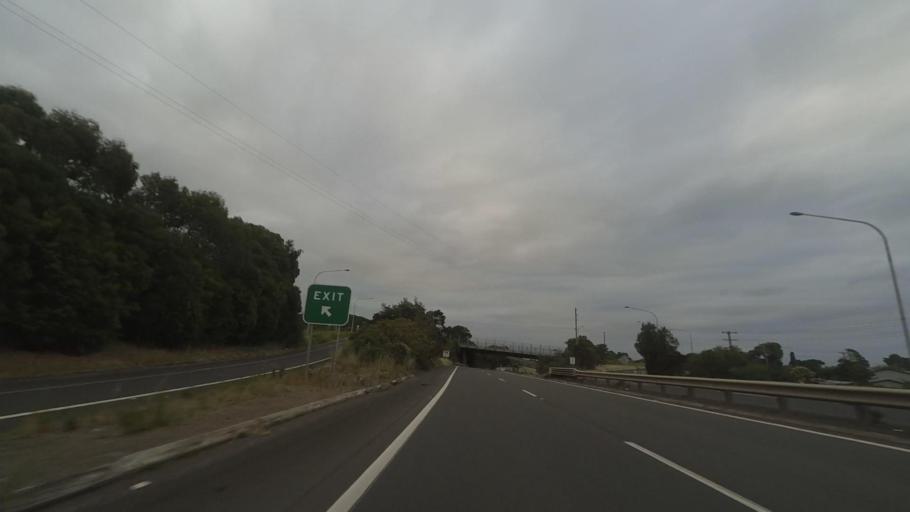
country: AU
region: New South Wales
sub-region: Kiama
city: Kiama
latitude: -34.6986
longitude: 150.8427
